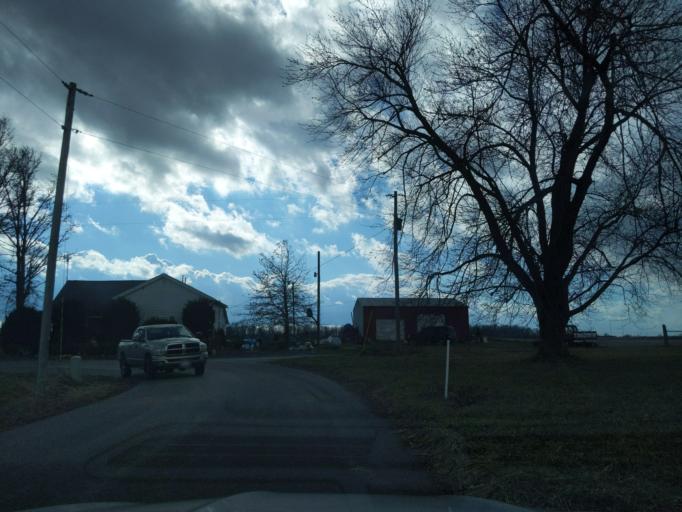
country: US
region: Indiana
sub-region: Decatur County
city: Greensburg
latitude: 39.3733
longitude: -85.5034
